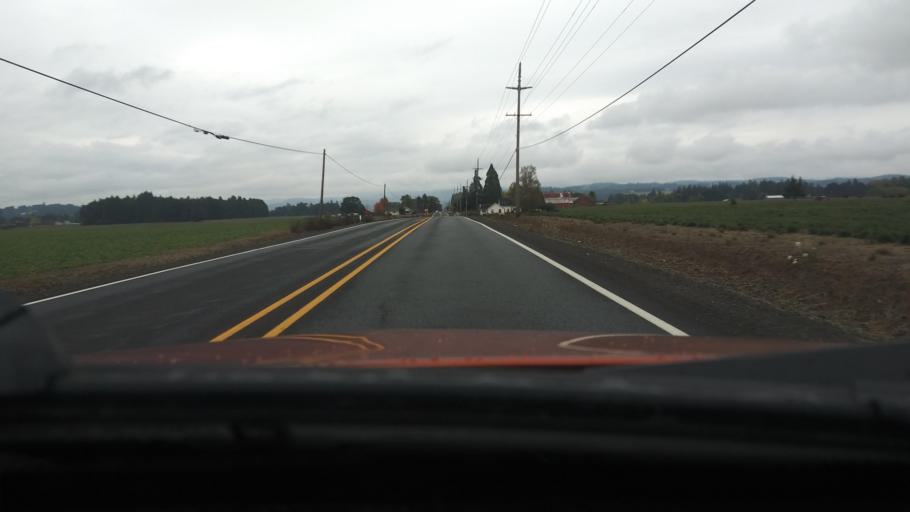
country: US
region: Oregon
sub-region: Washington County
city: Banks
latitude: 45.5940
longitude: -123.1145
